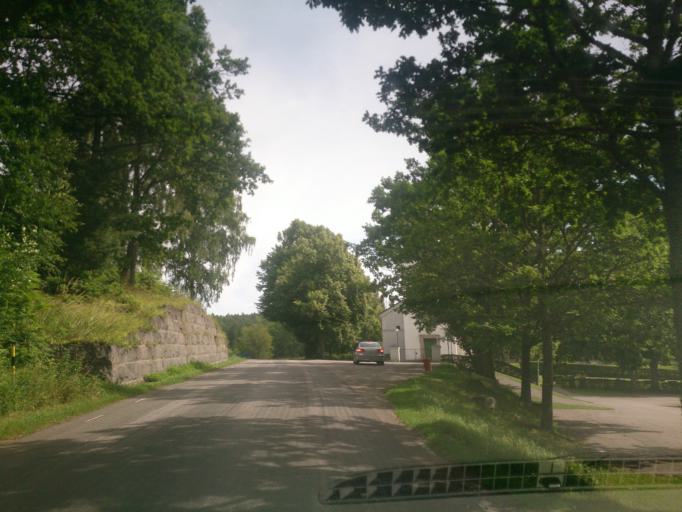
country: SE
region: OEstergoetland
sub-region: Soderkopings Kommun
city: Soederkoeping
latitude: 58.2815
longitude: 16.2175
